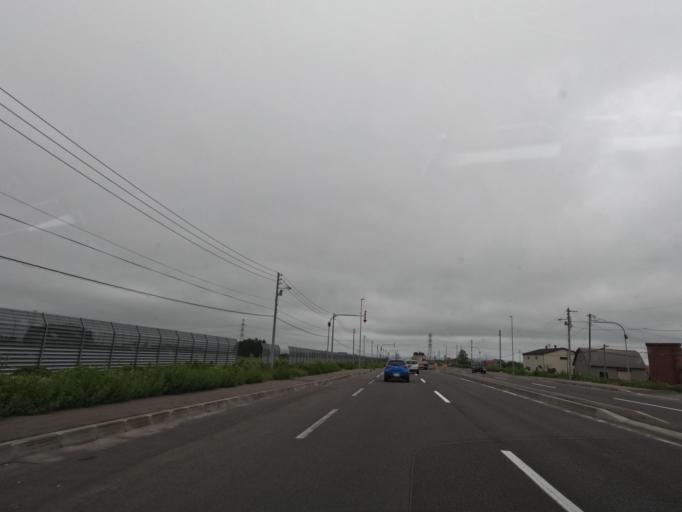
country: JP
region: Hokkaido
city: Ebetsu
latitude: 43.1547
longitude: 141.5184
